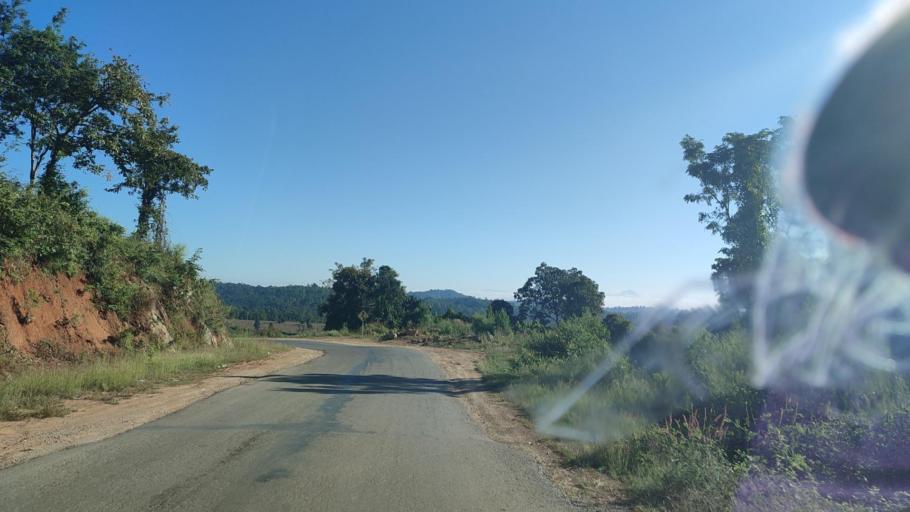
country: MM
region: Shan
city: Taunggyi
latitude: 20.9375
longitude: 97.6079
